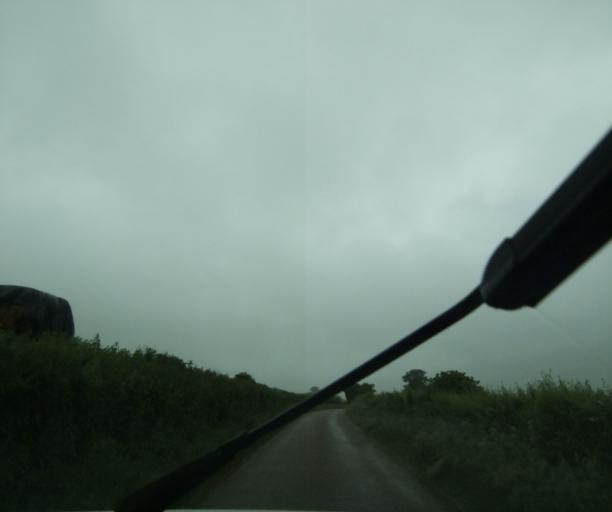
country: FR
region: Bourgogne
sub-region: Departement de Saone-et-Loire
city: Charolles
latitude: 46.3896
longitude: 4.2947
